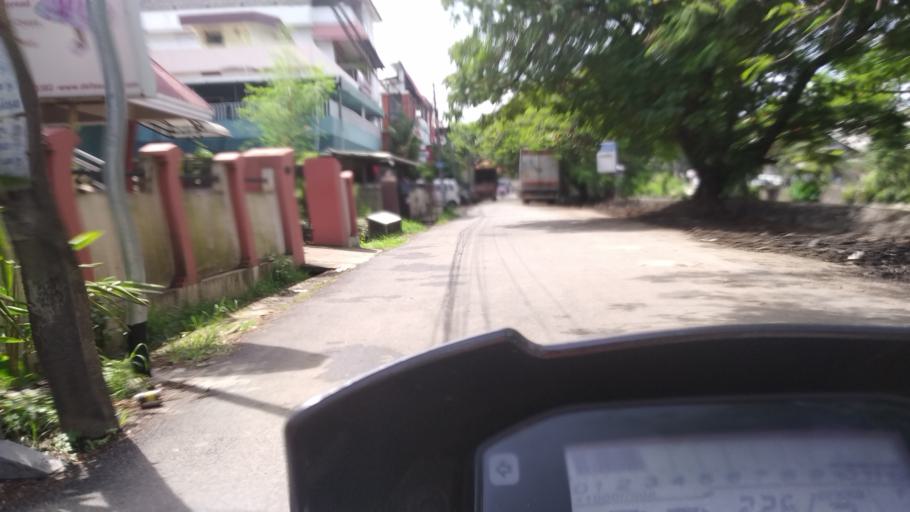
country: IN
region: Kerala
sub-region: Ernakulam
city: Cochin
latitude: 9.9640
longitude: 76.2978
